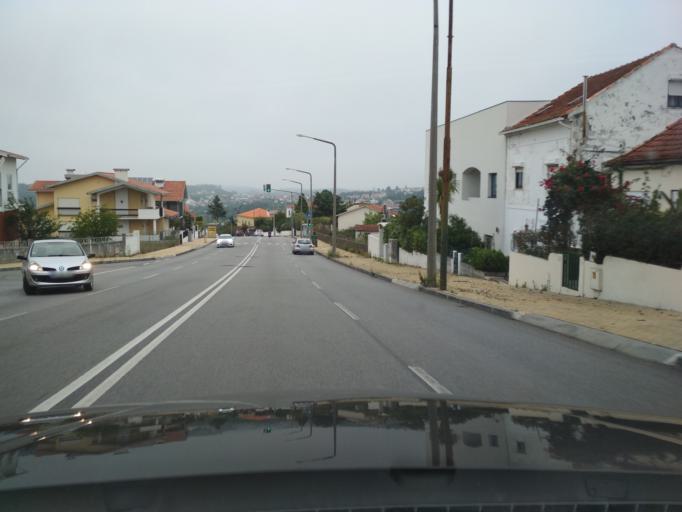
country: PT
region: Coimbra
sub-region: Coimbra
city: Coimbra
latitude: 40.2206
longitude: -8.4072
